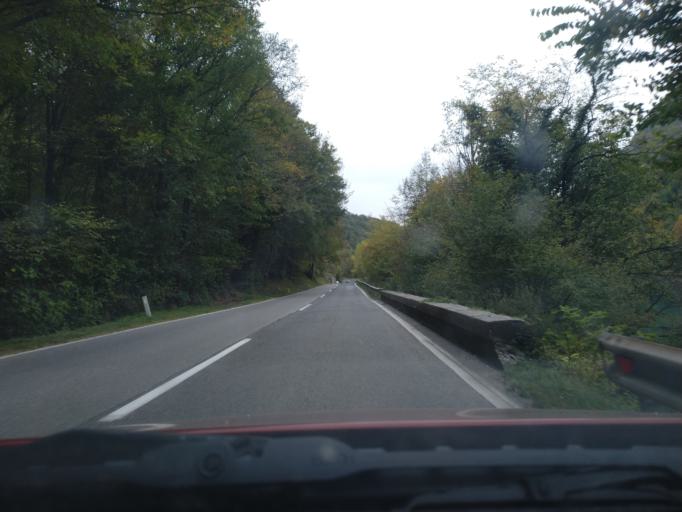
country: SI
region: Nova Gorica
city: Solkan
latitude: 46.0066
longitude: 13.6256
